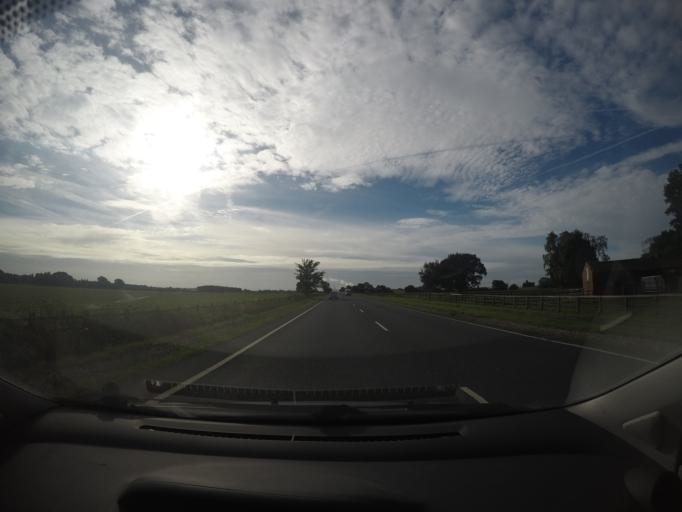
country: GB
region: England
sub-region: North Yorkshire
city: Riccall
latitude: 53.8208
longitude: -1.0460
